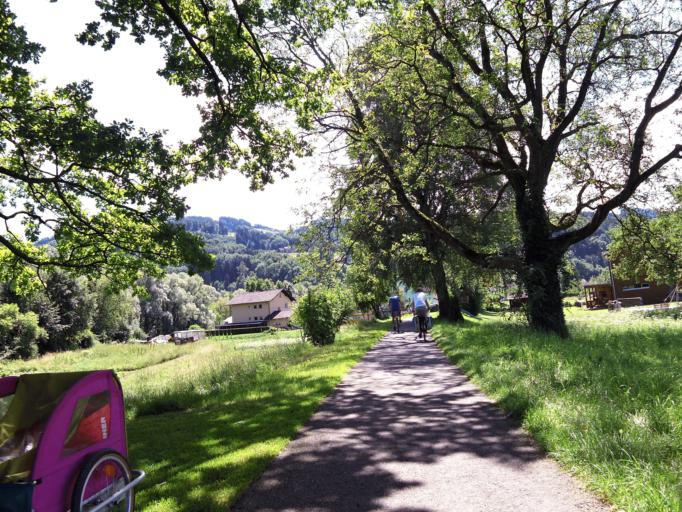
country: AT
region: Vorarlberg
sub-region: Politischer Bezirk Bregenz
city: Gaissau
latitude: 47.4644
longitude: 9.6042
